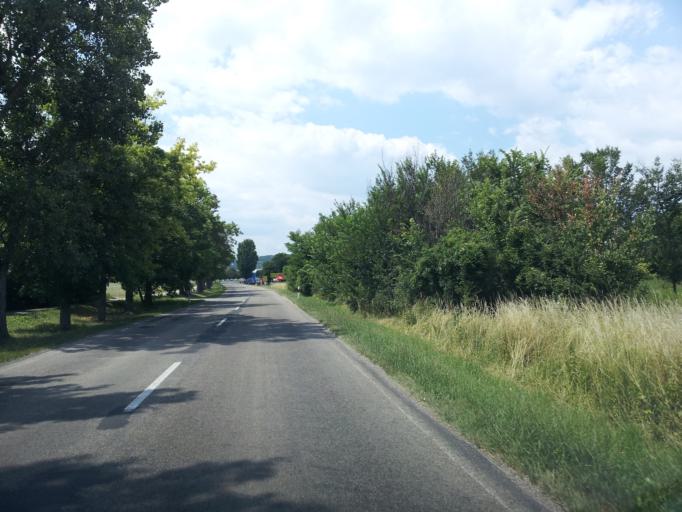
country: HU
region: Veszprem
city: Tihany
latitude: 46.9219
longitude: 17.8485
